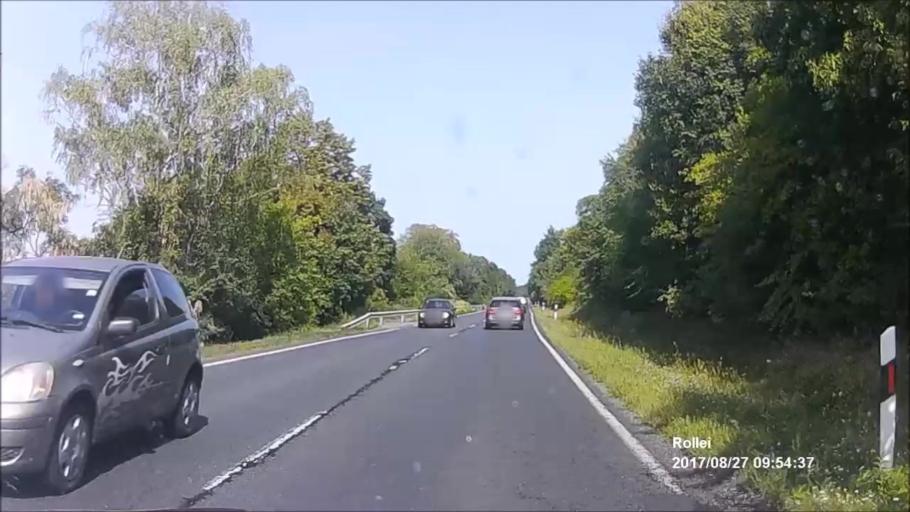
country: AT
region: Burgenland
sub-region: Eisenstadt-Umgebung
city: Klingenbach
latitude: 47.7241
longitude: 16.5618
